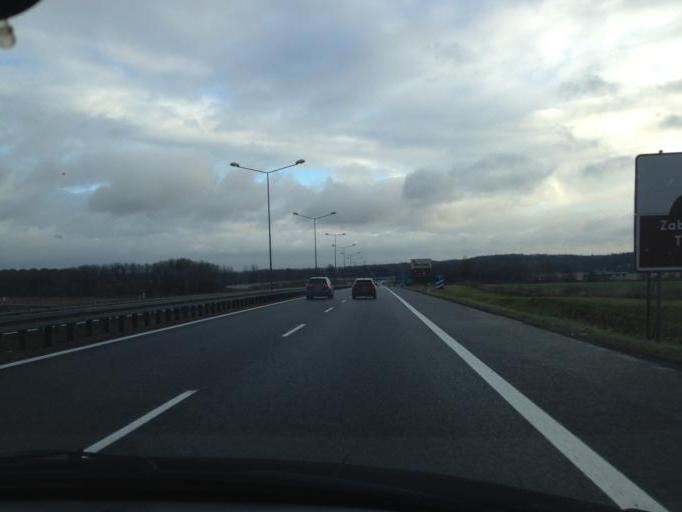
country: PL
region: Silesian Voivodeship
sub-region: Powiat gliwicki
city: Rudziniec
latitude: 50.3955
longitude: 18.4402
